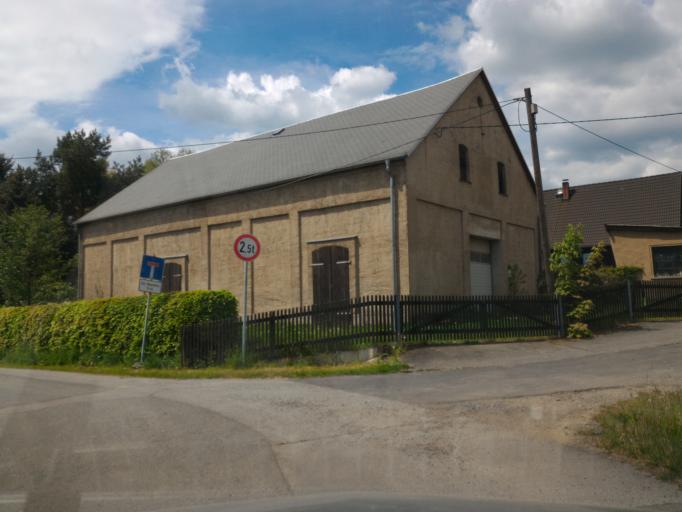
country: DE
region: Saxony
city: Seifhennersdorf
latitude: 50.9377
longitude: 14.6186
